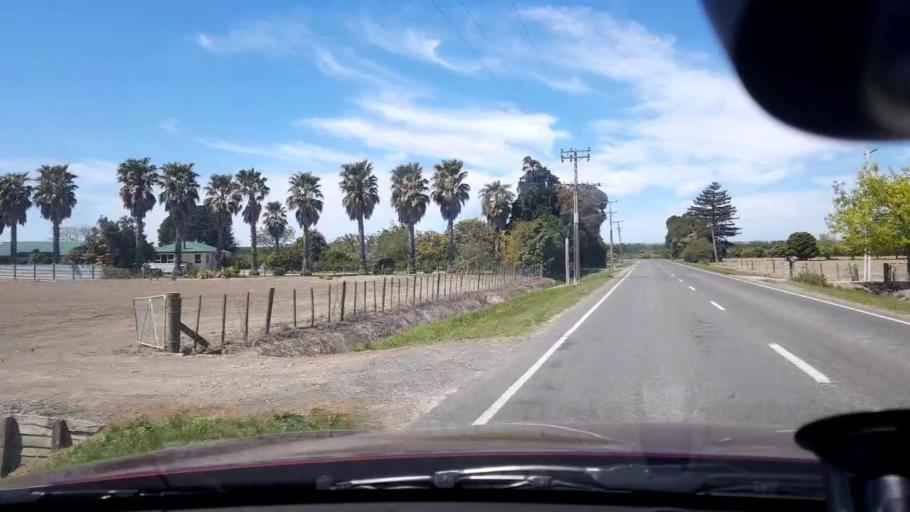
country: NZ
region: Gisborne
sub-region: Gisborne District
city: Gisborne
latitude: -38.6360
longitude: 177.9304
